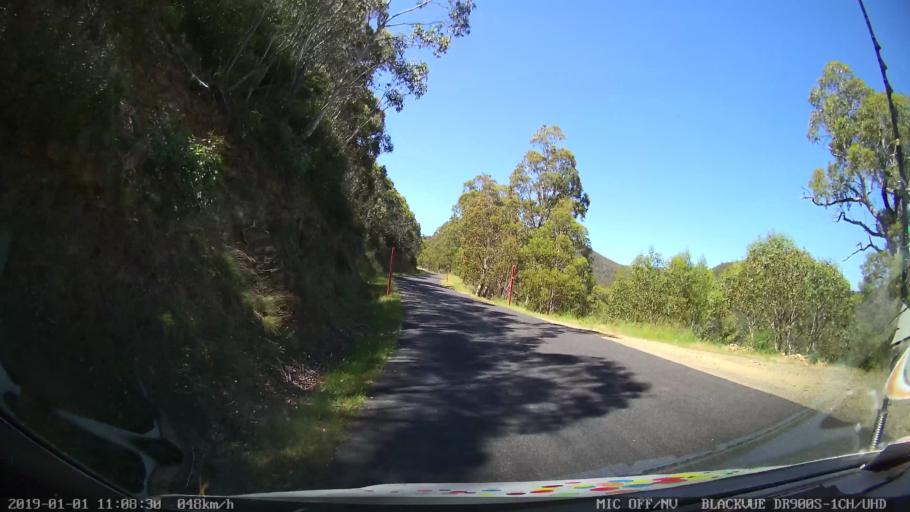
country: AU
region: New South Wales
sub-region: Snowy River
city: Jindabyne
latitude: -35.9600
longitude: 148.3946
